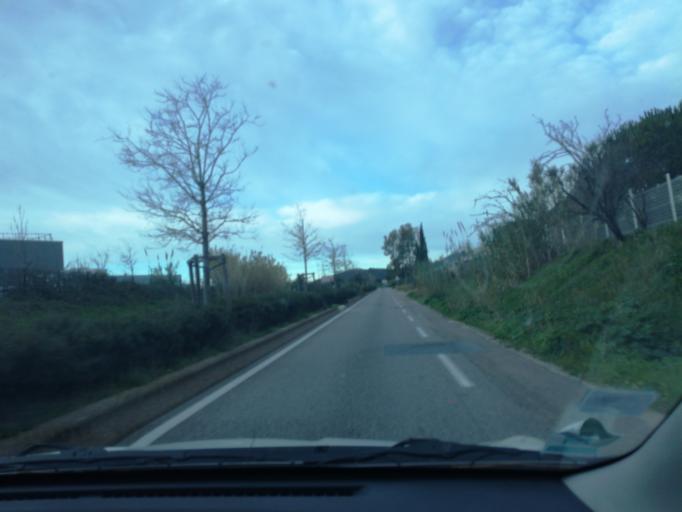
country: FR
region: Provence-Alpes-Cote d'Azur
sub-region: Departement du Var
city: La Farlede
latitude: 43.1595
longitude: 6.0535
